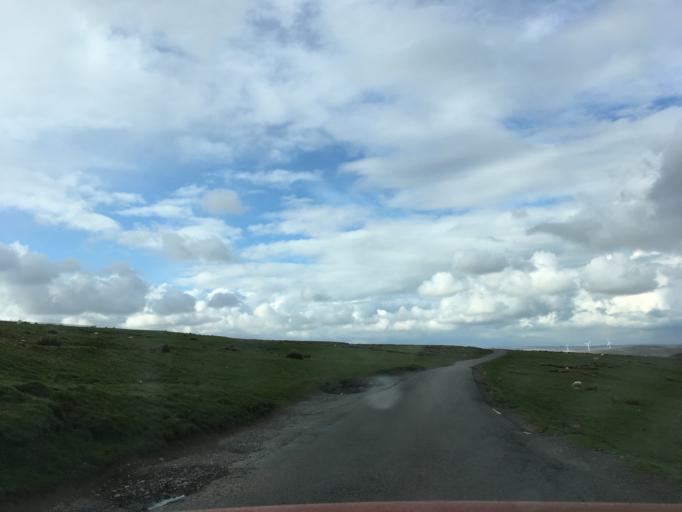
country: GB
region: Wales
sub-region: Caerphilly County Borough
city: Rhymney
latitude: 51.7244
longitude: -3.2977
